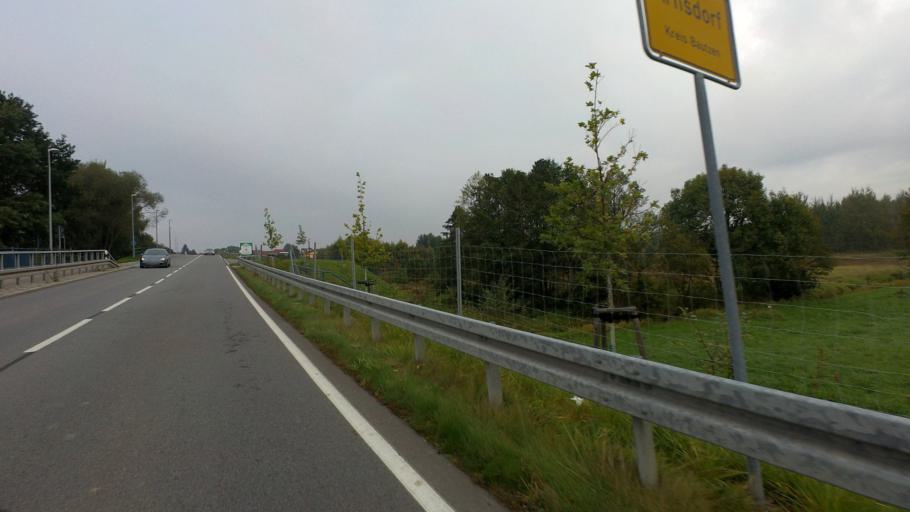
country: DE
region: Saxony
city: Arnsdorf
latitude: 51.0899
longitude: 14.0093
